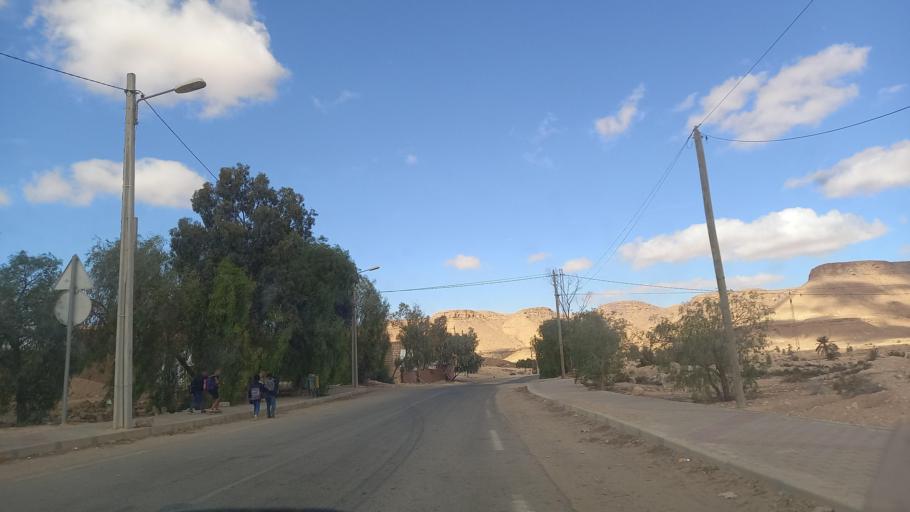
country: TN
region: Tataouine
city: Tataouine
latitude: 32.9148
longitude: 10.2784
